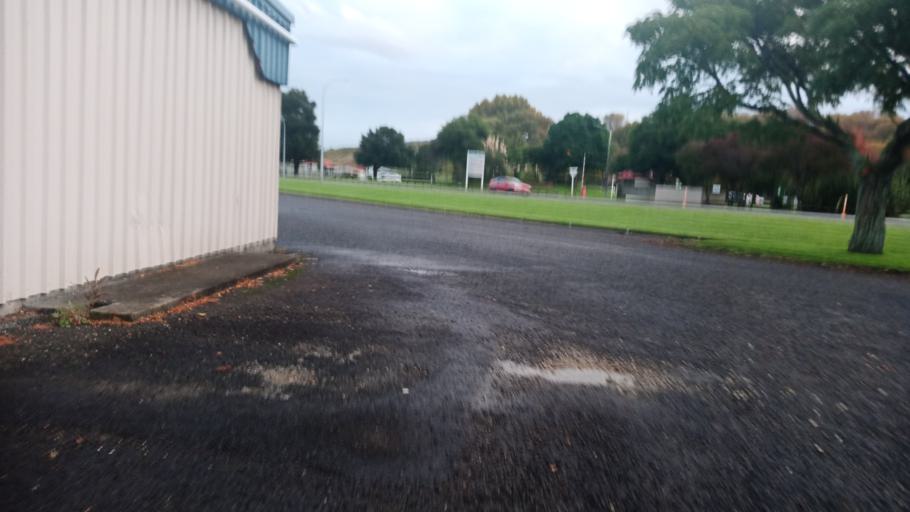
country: NZ
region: Gisborne
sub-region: Gisborne District
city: Gisborne
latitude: -38.6395
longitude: 178.0029
